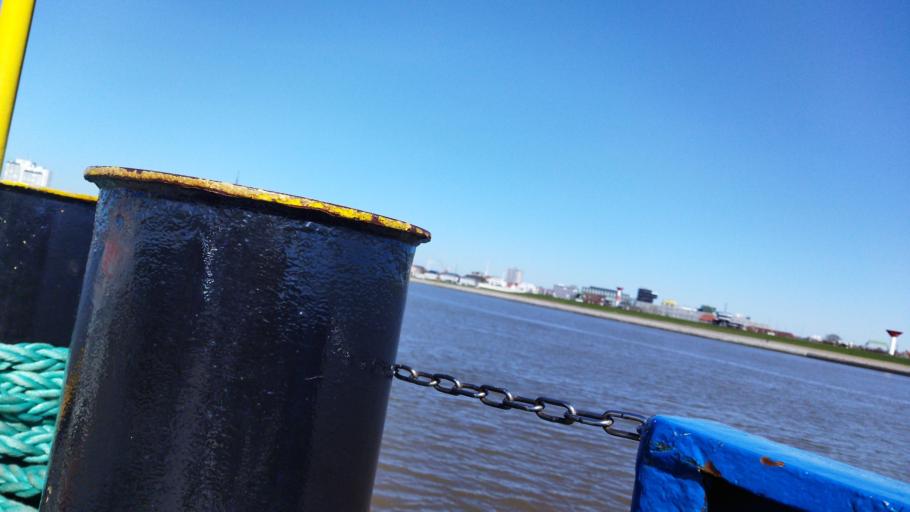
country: DE
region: Bremen
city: Bremerhaven
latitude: 53.5316
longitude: 8.5699
